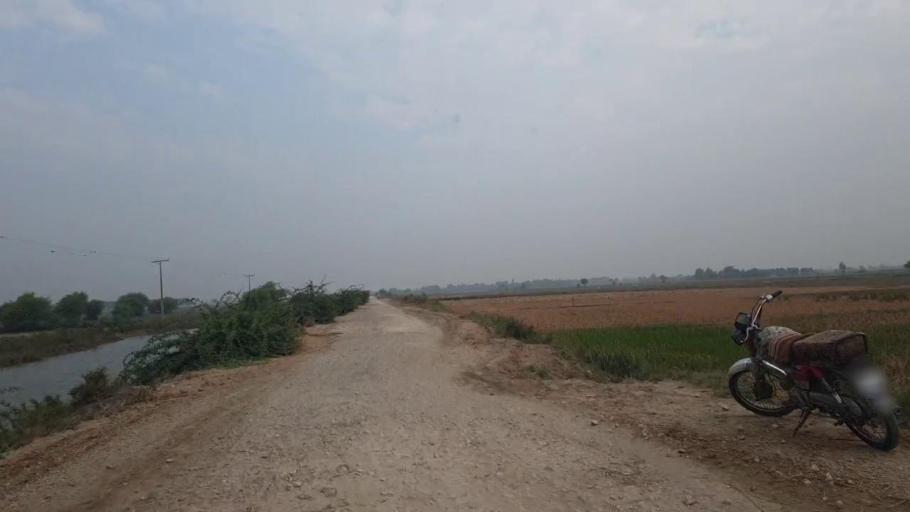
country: PK
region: Sindh
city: Talhar
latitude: 24.8177
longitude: 68.8770
